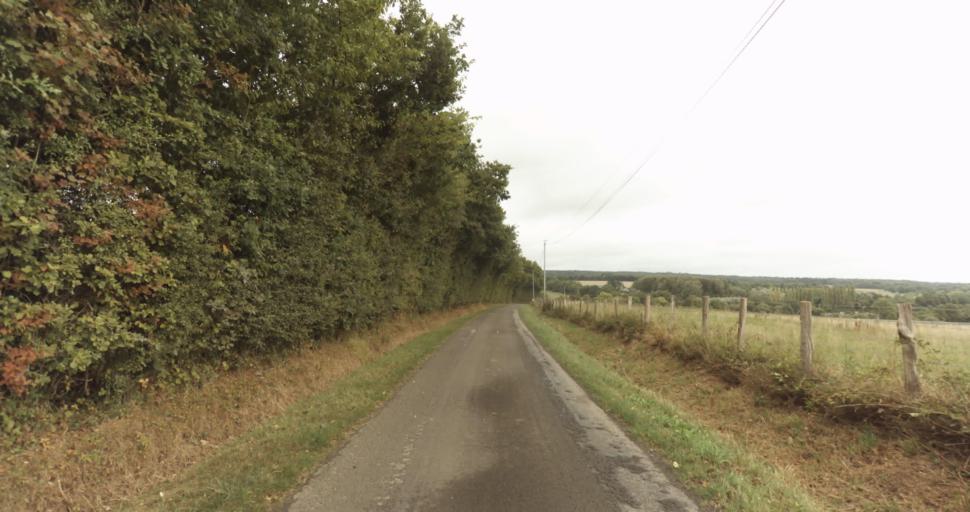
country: FR
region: Lower Normandy
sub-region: Departement de l'Orne
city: Sainte-Gauburge-Sainte-Colombe
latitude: 48.7259
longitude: 0.4783
